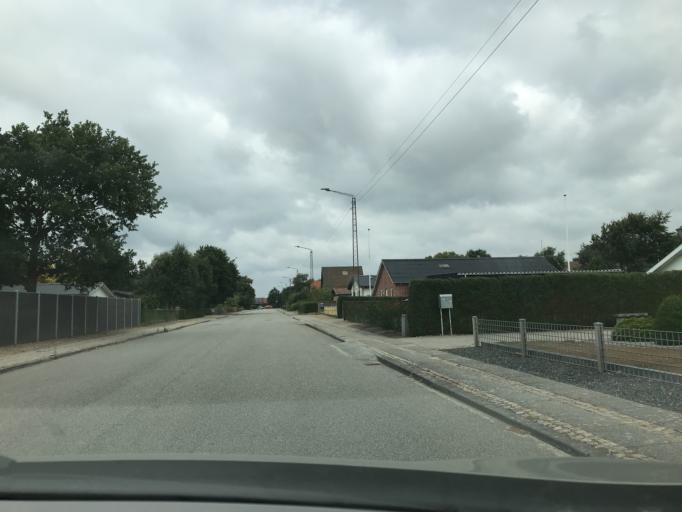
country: DK
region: Central Jutland
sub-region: Ringkobing-Skjern Kommune
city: Tarm
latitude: 55.9017
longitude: 8.5126
